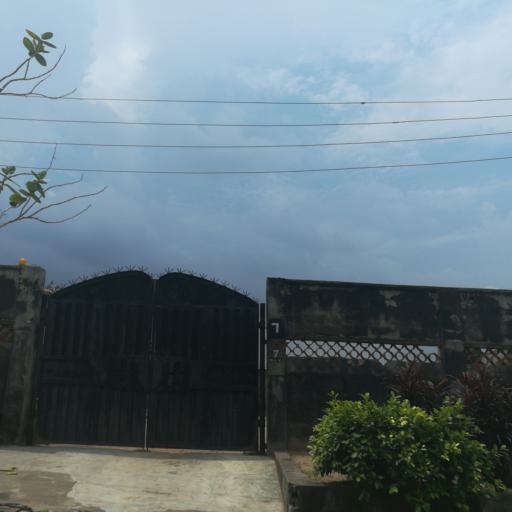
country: NG
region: Lagos
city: Ojota
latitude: 6.5736
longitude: 3.3853
